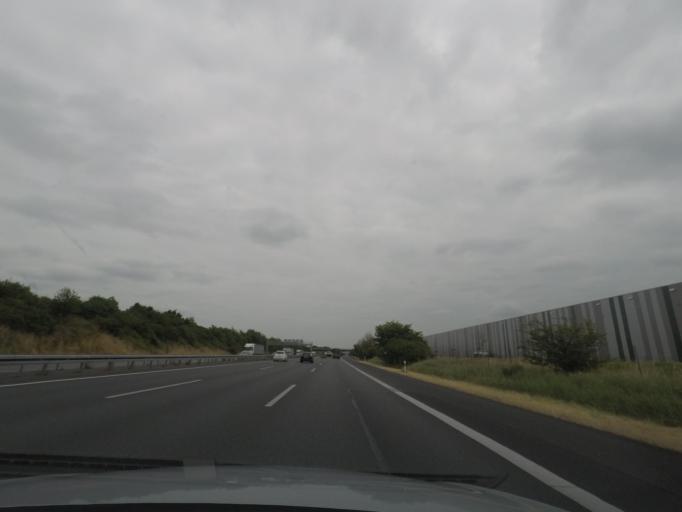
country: DE
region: Lower Saxony
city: Arpke
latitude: 52.3628
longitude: 10.1306
